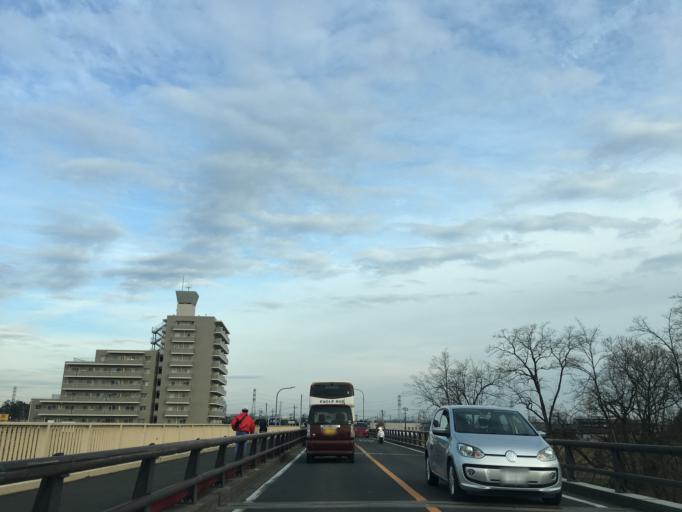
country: JP
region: Saitama
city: Kawagoe
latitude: 35.9188
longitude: 139.4523
